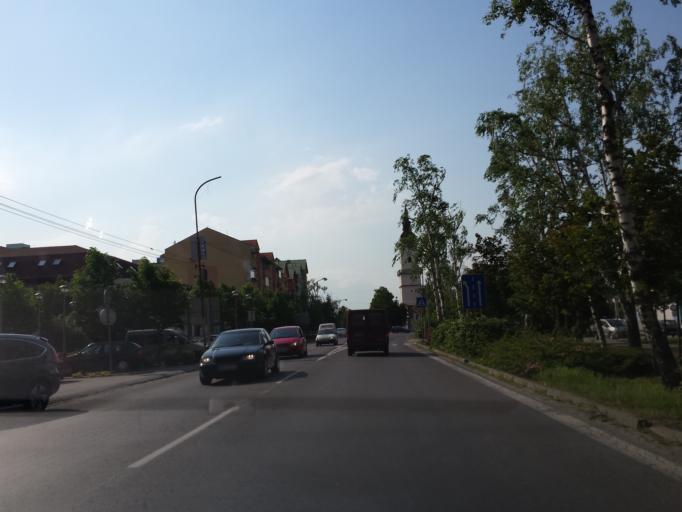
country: SK
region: Bratislavsky
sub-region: Okres Malacky
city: Malacky
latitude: 48.4394
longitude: 17.0139
